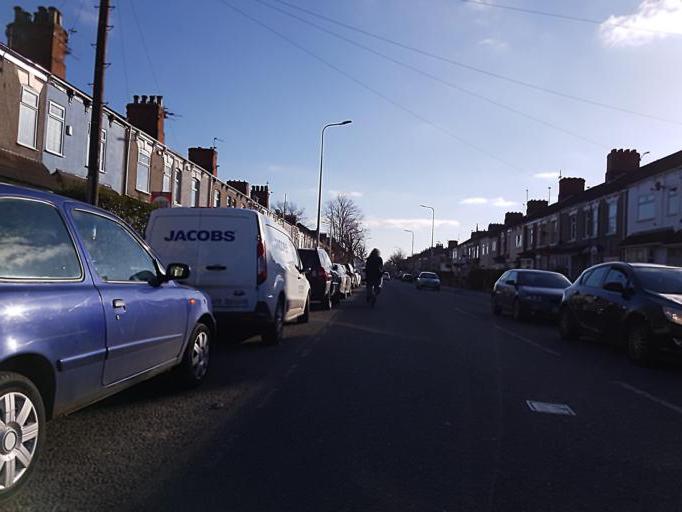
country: GB
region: England
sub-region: North East Lincolnshire
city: Grimsby
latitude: 53.5652
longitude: -0.0753
